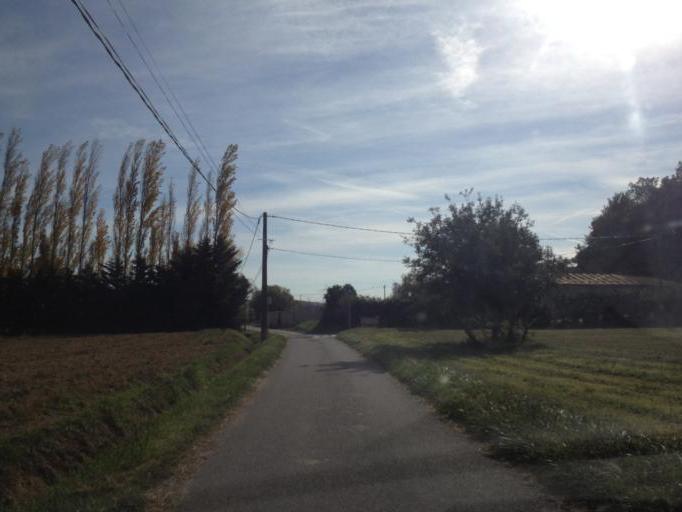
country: FR
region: Provence-Alpes-Cote d'Azur
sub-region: Departement du Vaucluse
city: Bedarrides
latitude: 44.0520
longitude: 4.8931
